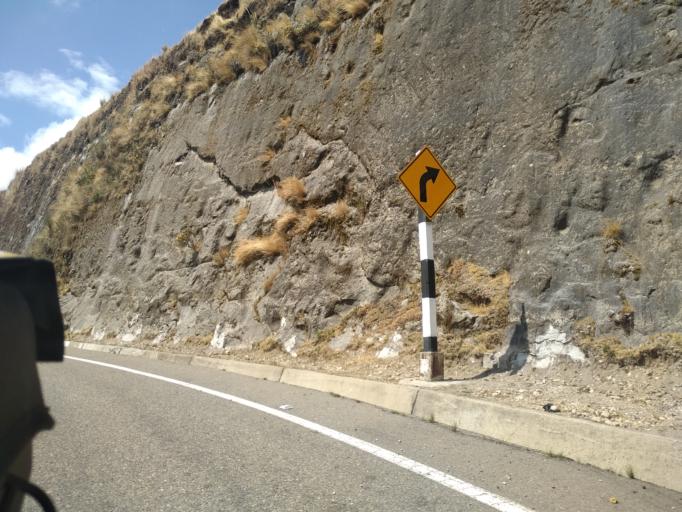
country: PE
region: La Libertad
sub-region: Provincia de Santiago de Chuco
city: Quiruvilca
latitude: -7.9184
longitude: -78.1533
